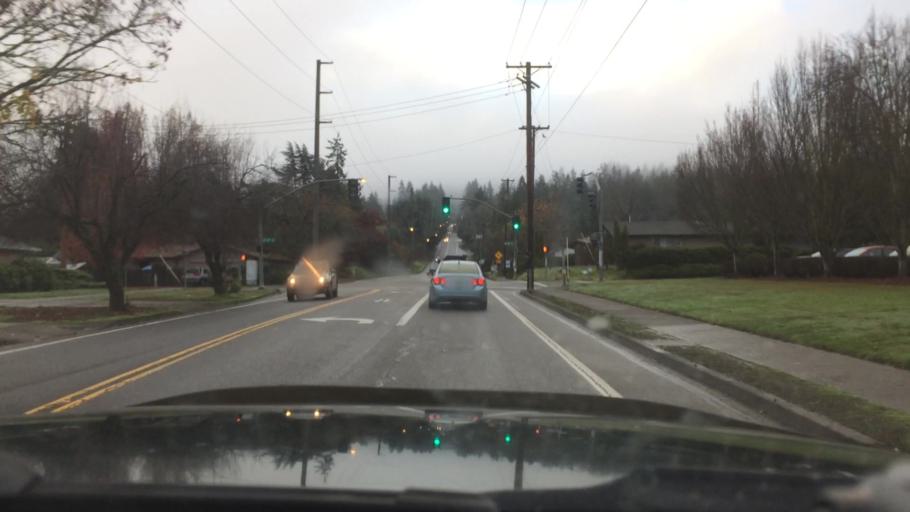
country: US
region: Oregon
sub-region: Lane County
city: Eugene
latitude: 44.0337
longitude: -123.1179
